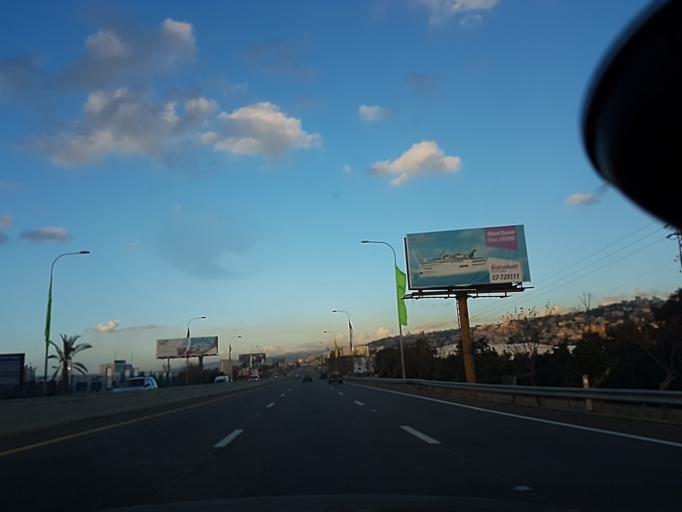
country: LB
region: Liban-Sud
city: Sidon
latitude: 33.5061
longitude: 35.3501
